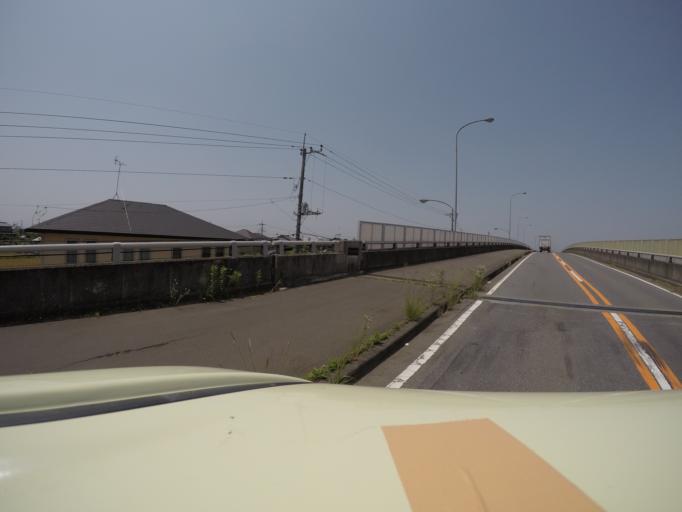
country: JP
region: Ibaraki
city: Mitsukaido
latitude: 36.0364
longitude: 139.9935
